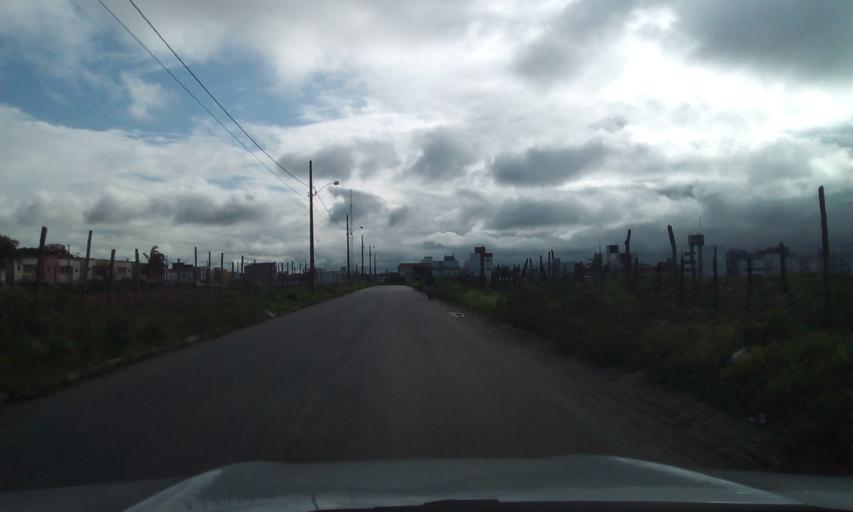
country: BR
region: Paraiba
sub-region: Conde
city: Conde
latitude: -7.2132
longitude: -34.8465
